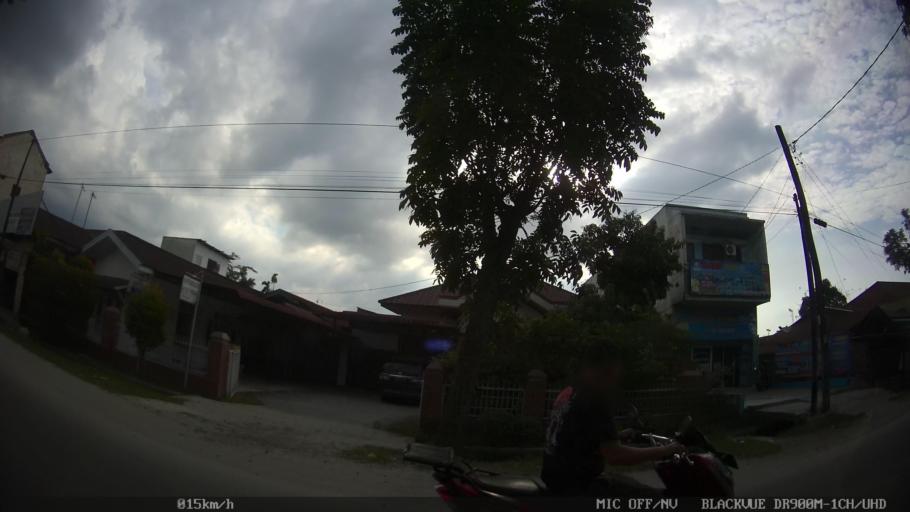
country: ID
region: North Sumatra
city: Sunggal
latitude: 3.5593
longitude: 98.6171
